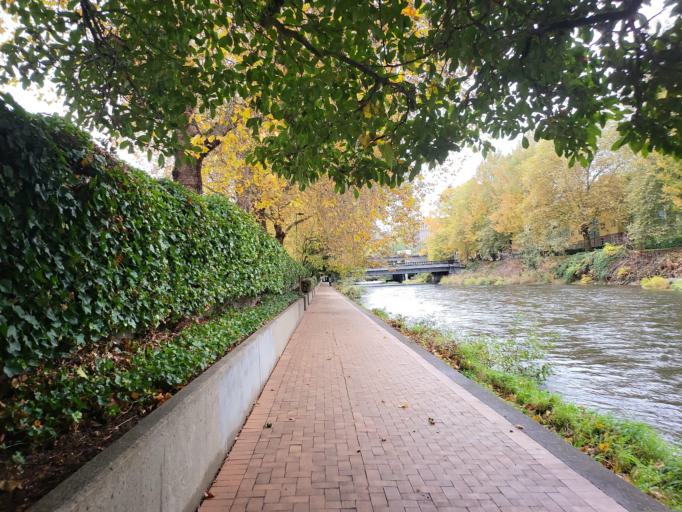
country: US
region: Washington
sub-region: King County
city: Renton
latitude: 47.4832
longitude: -122.2041
